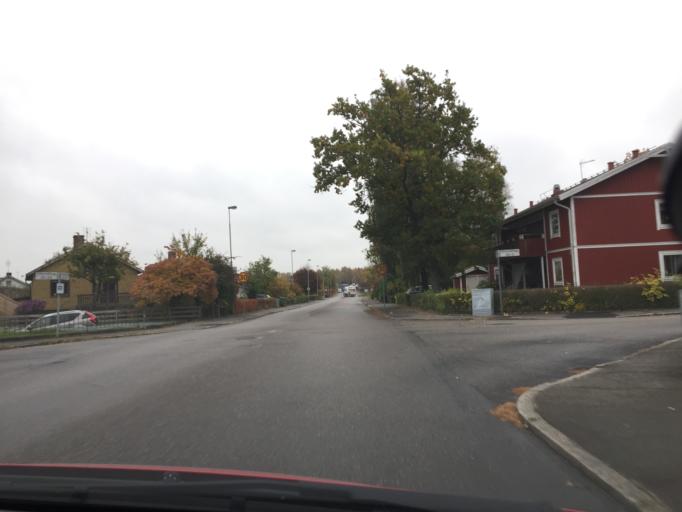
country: SE
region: Vaestra Goetaland
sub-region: Trollhattan
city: Trollhattan
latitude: 58.2822
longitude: 12.3158
